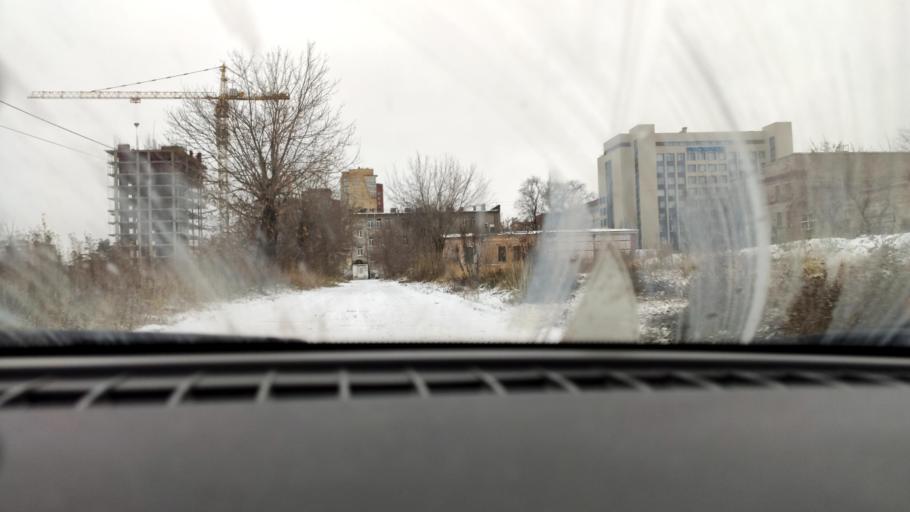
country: RU
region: Perm
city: Perm
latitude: 57.9909
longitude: 56.2090
